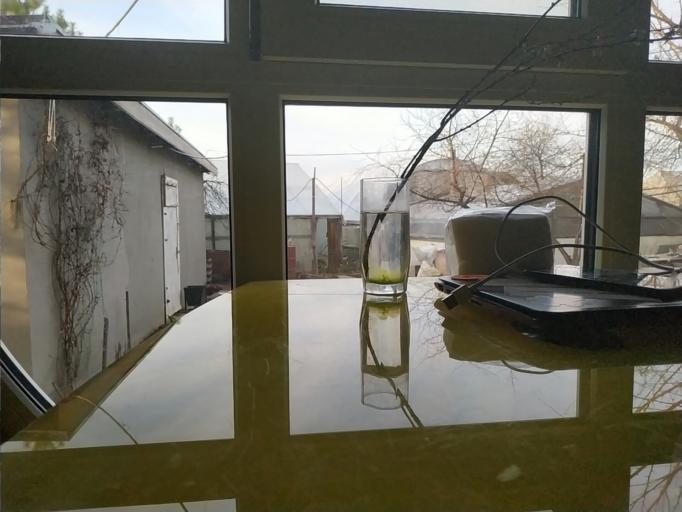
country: RU
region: Republic of Karelia
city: Suoyarvi
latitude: 62.1310
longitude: 32.1498
